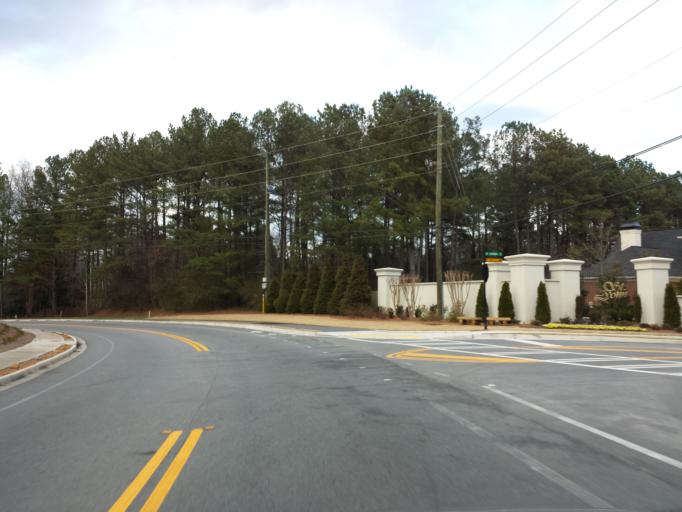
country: US
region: Georgia
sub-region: Fulton County
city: Sandy Springs
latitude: 33.9735
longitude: -84.3907
